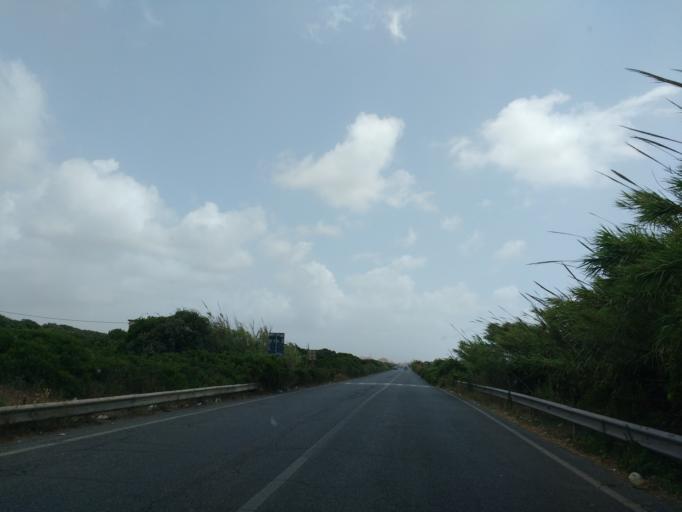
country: IT
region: Latium
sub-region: Citta metropolitana di Roma Capitale
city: Torvaianica
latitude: 41.6545
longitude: 12.4199
